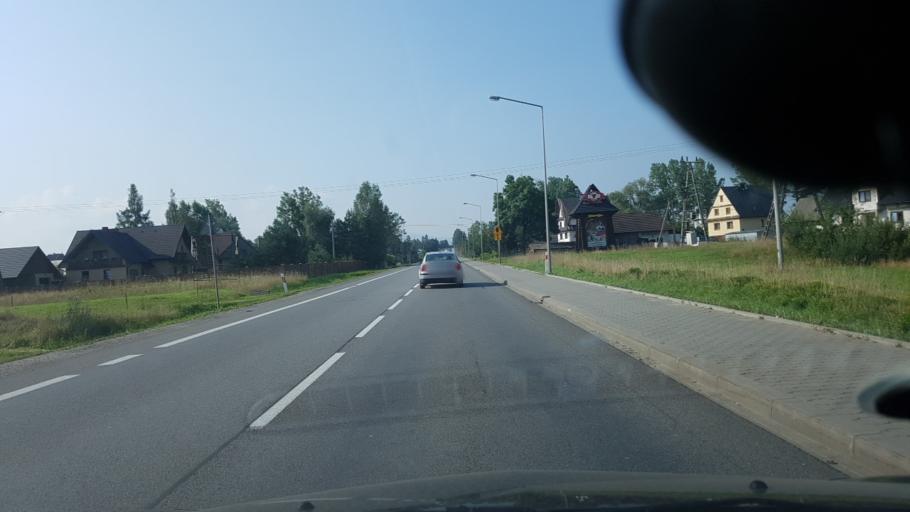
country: PL
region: Lesser Poland Voivodeship
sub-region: Powiat nowotarski
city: Jablonka
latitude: 49.4665
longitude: 19.6916
